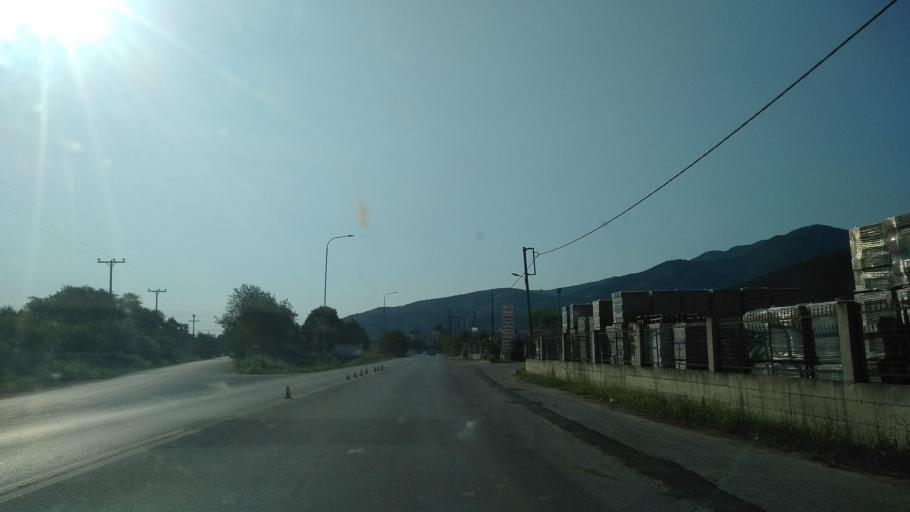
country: GR
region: Central Macedonia
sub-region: Nomos Thessalonikis
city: Stavros
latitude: 40.6678
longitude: 23.6819
